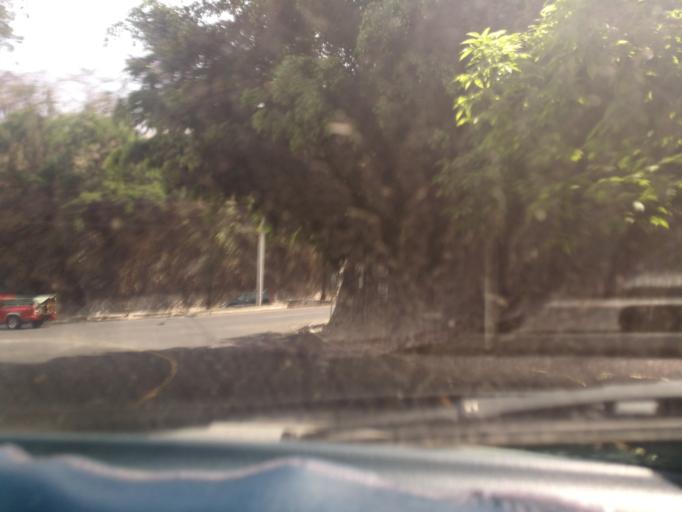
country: GT
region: Guatemala
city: Guatemala City
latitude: 14.6255
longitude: -90.4823
